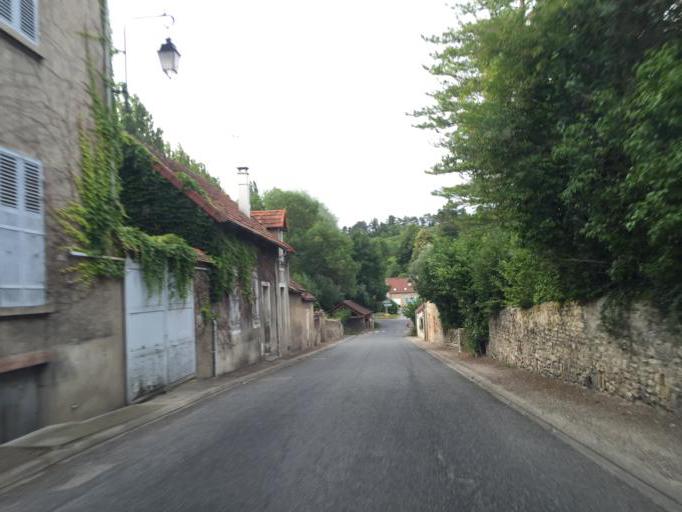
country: FR
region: Auvergne
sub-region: Departement de l'Allier
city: Saint-Germain-des-Fosses
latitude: 46.2368
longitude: 3.4306
